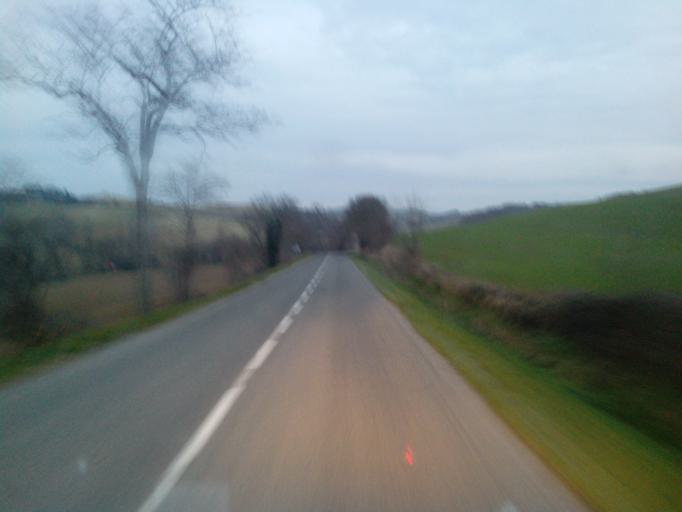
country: FR
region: Midi-Pyrenees
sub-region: Departement de l'Ariege
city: Mazeres
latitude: 43.2754
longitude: 1.7486
